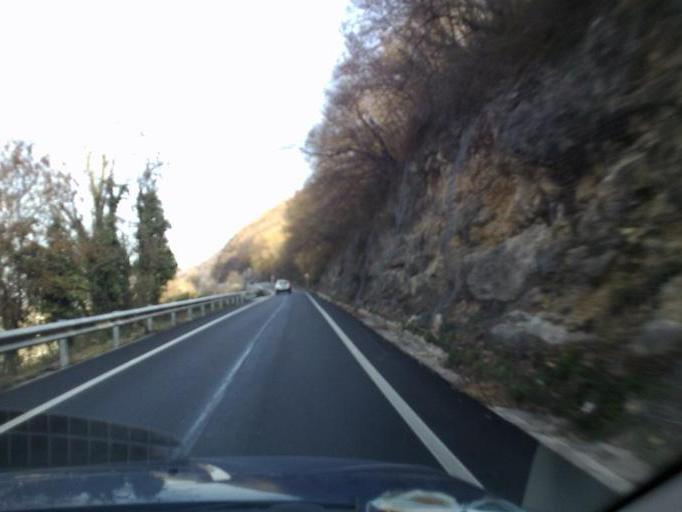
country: IT
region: Veneto
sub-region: Provincia di Verona
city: Grezzana
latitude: 45.5378
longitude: 11.0060
